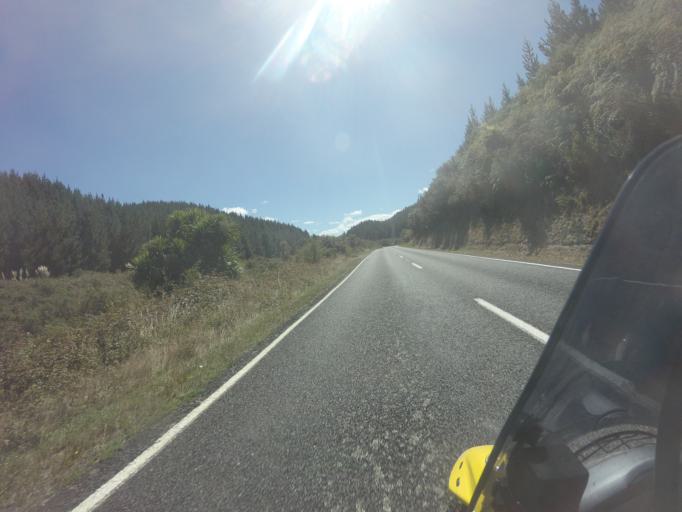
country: NZ
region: Bay of Plenty
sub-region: Whakatane District
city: Murupara
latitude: -38.2915
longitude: 176.8124
